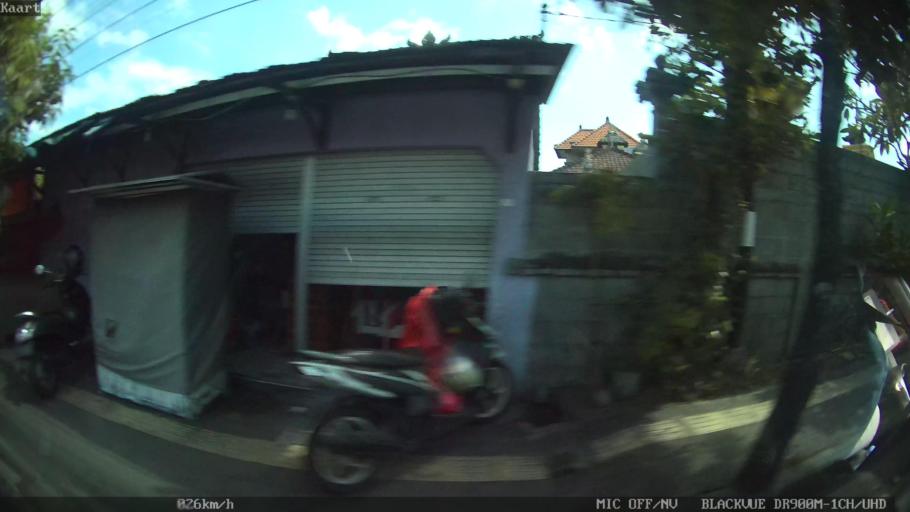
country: ID
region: Bali
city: Banjar Kertasari
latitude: -8.6308
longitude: 115.1827
